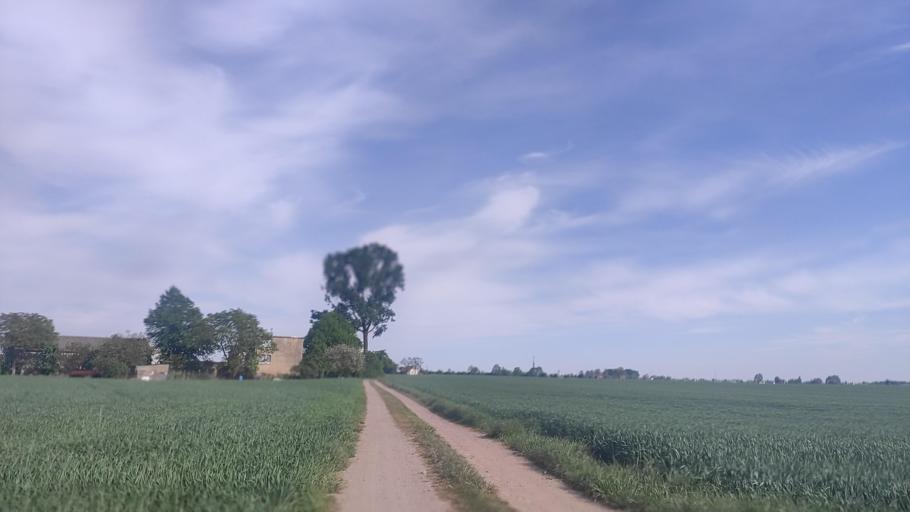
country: PL
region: Greater Poland Voivodeship
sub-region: Powiat poznanski
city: Swarzedz
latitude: 52.4184
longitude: 17.1453
